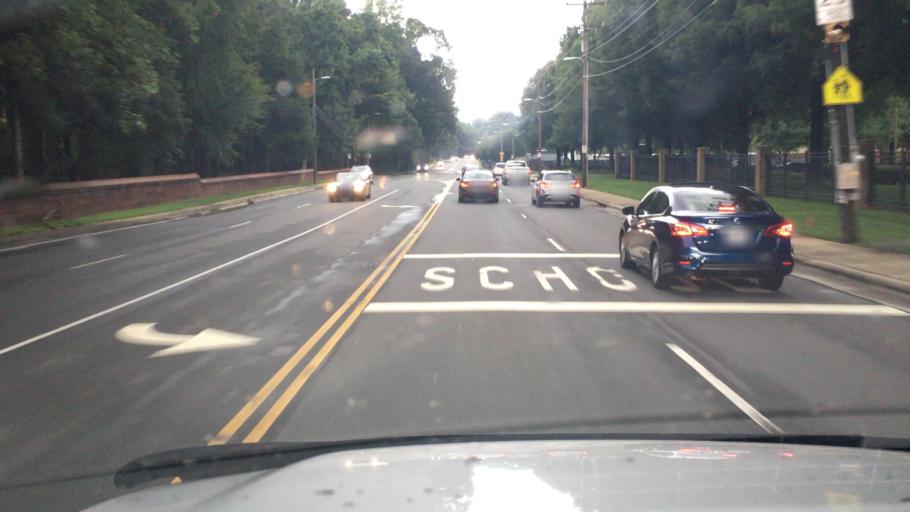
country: US
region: North Carolina
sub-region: Mecklenburg County
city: Matthews
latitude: 35.1481
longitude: -80.8020
